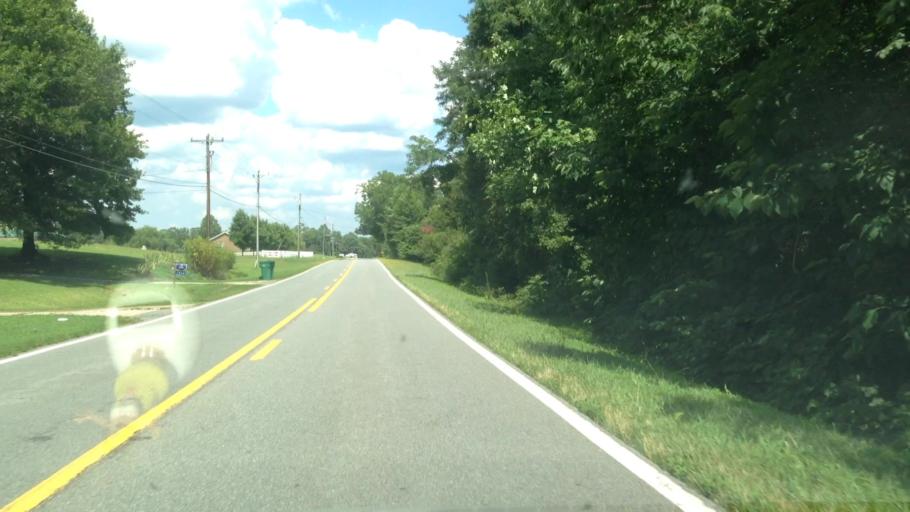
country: US
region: North Carolina
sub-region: Rockingham County
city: Reidsville
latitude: 36.4096
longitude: -79.6146
